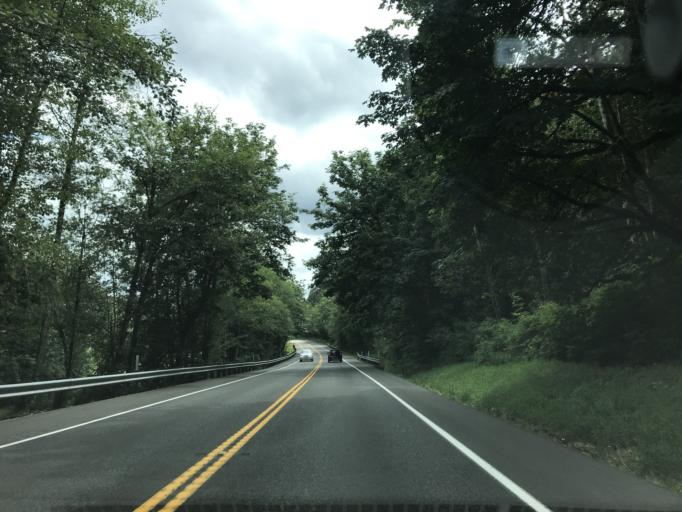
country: US
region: Washington
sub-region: King County
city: Maple Valley
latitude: 47.4167
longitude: -122.0665
